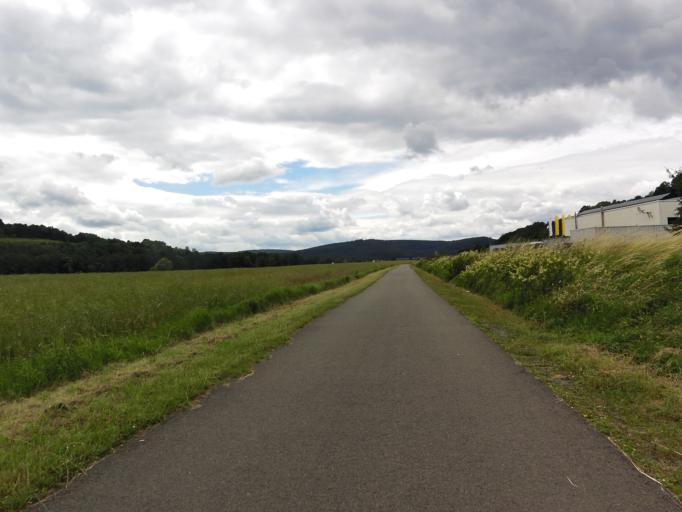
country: DE
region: Thuringia
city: Fambach
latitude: 50.7172
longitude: 10.3922
